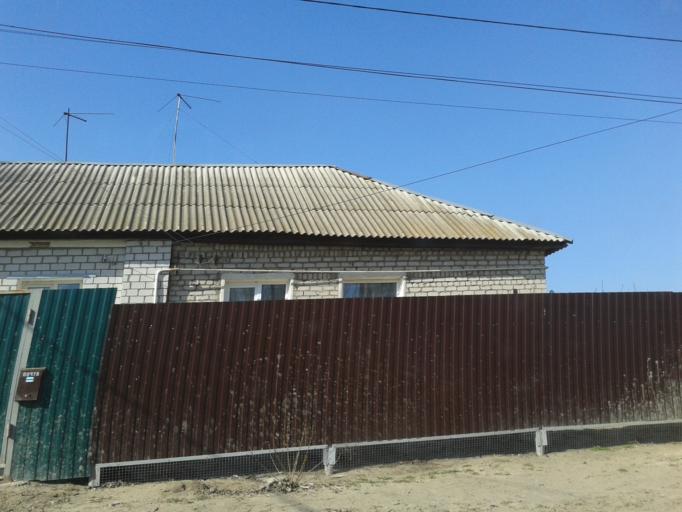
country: RU
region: Volgograd
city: Volgograd
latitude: 48.6305
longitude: 44.3936
